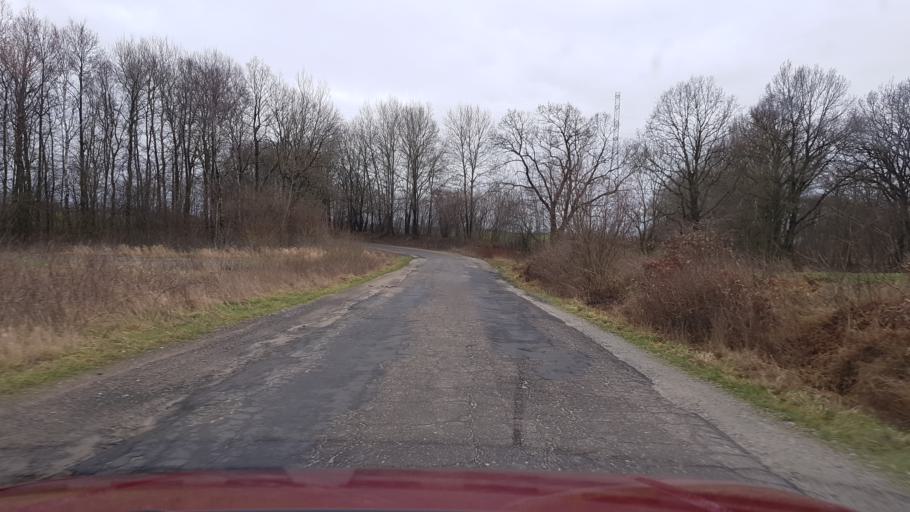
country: PL
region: West Pomeranian Voivodeship
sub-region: Powiat koszalinski
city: Mielno
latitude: 54.1486
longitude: 16.0302
